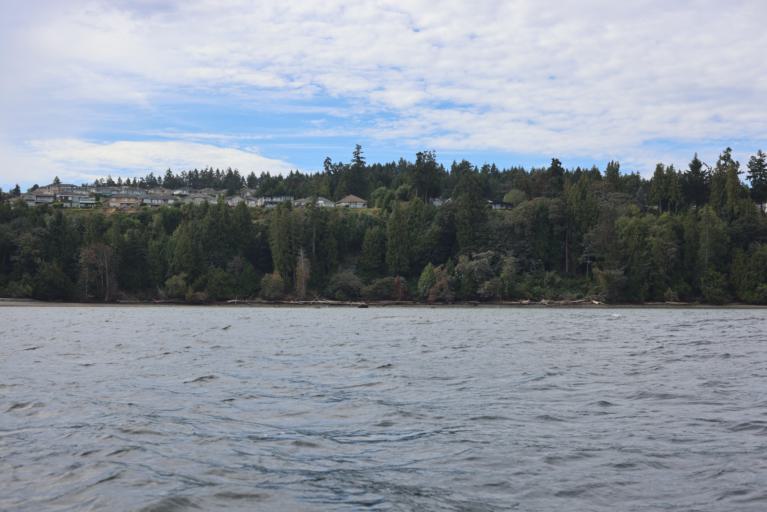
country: CA
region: British Columbia
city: Nanaimo
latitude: 49.2521
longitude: -124.0523
